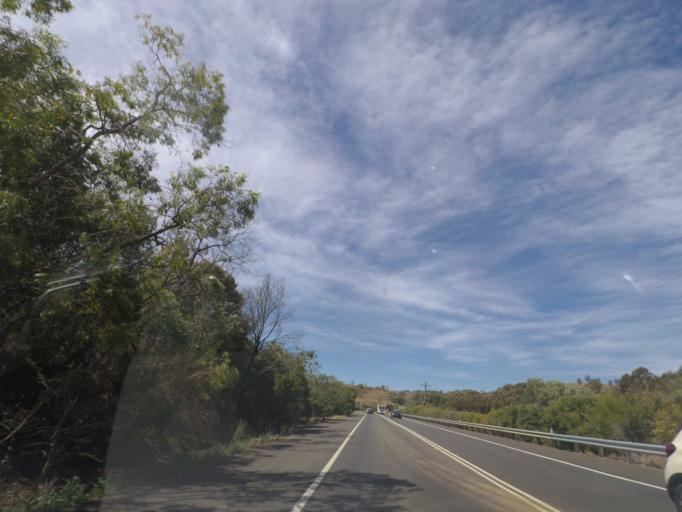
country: AU
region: New South Wales
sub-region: Wollondilly
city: Picton
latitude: -34.1598
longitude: 150.6509
